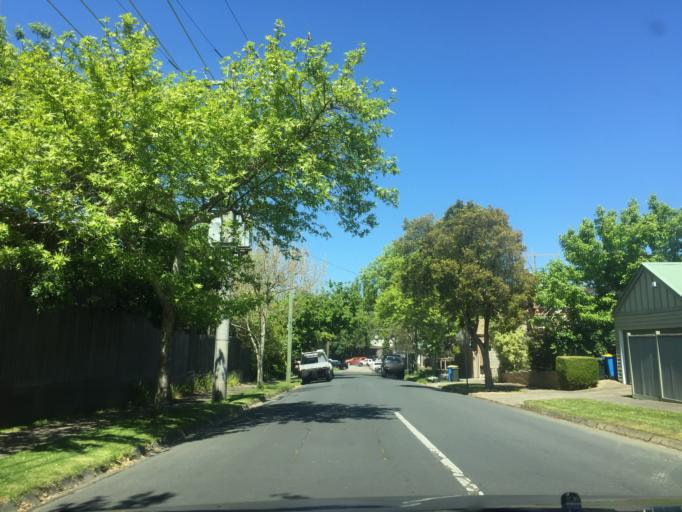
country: AU
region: Victoria
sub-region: Whitehorse
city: Surrey Hills
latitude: -37.8235
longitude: 145.0933
